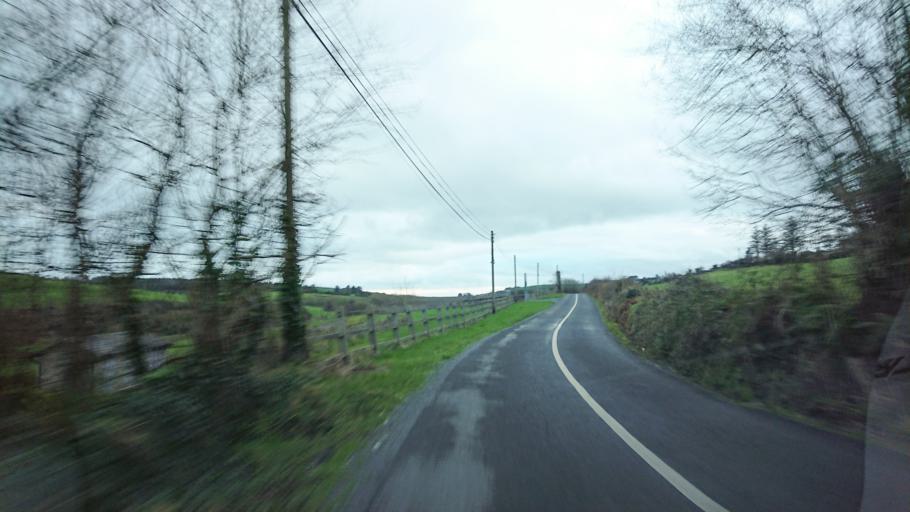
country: IE
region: Munster
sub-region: Waterford
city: Portlaw
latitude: 52.1616
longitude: -7.3854
